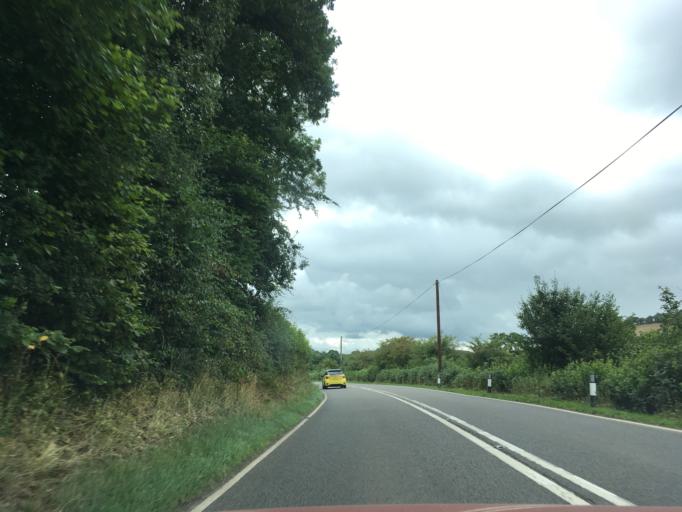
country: GB
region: Wales
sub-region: Carmarthenshire
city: Llandovery
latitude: 52.0025
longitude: -3.7594
